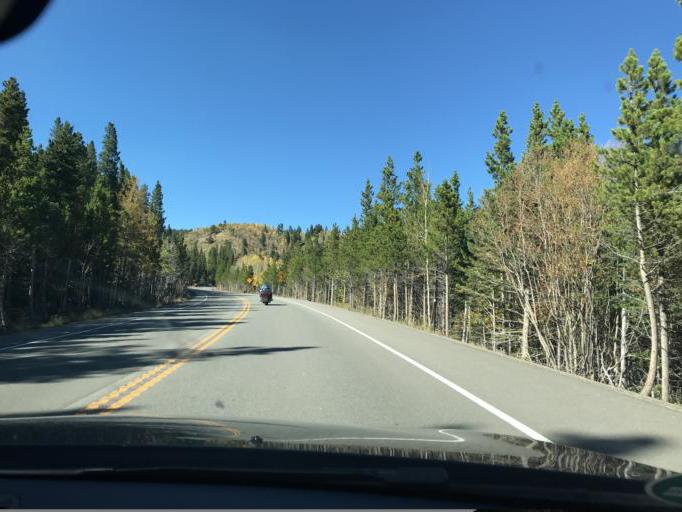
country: US
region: Colorado
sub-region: Boulder County
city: Nederland
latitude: 40.0665
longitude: -105.5154
